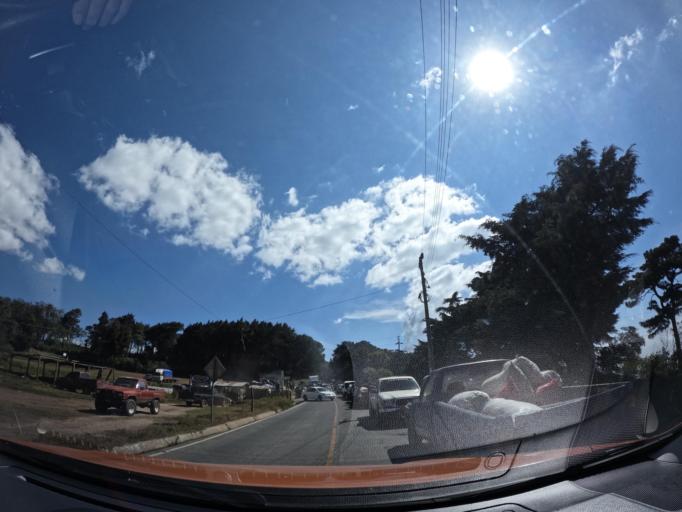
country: GT
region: Chimaltenango
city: Patzun
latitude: 14.6525
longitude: -91.0474
